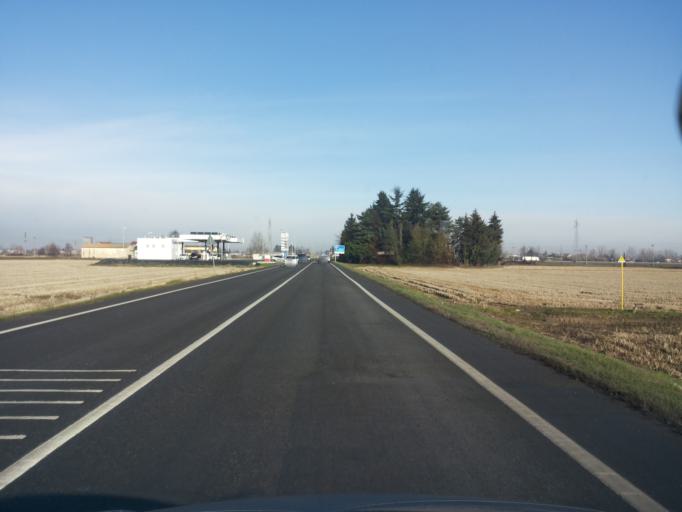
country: IT
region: Piedmont
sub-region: Provincia di Vercelli
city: Caresanablot
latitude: 45.3377
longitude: 8.3928
